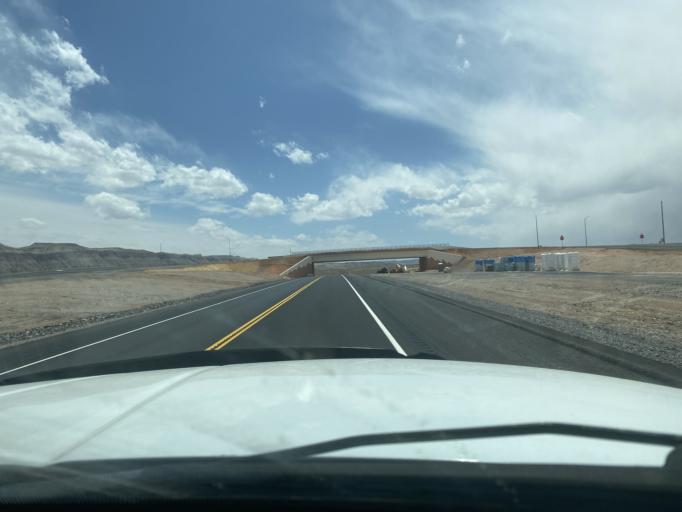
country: US
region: Utah
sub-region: Washington County
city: Hurricane
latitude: 37.1287
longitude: -113.3462
